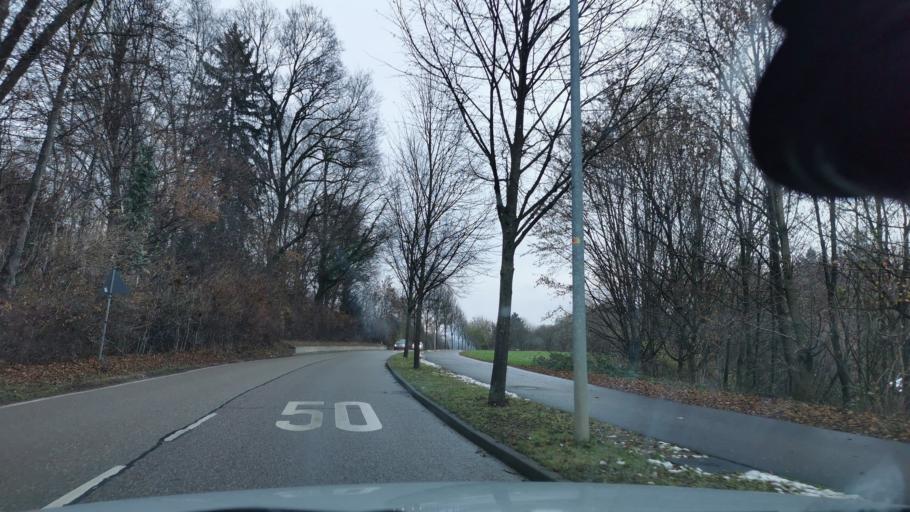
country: DE
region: Baden-Wuerttemberg
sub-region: Regierungsbezirk Stuttgart
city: Goeppingen
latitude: 48.7054
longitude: 9.6777
